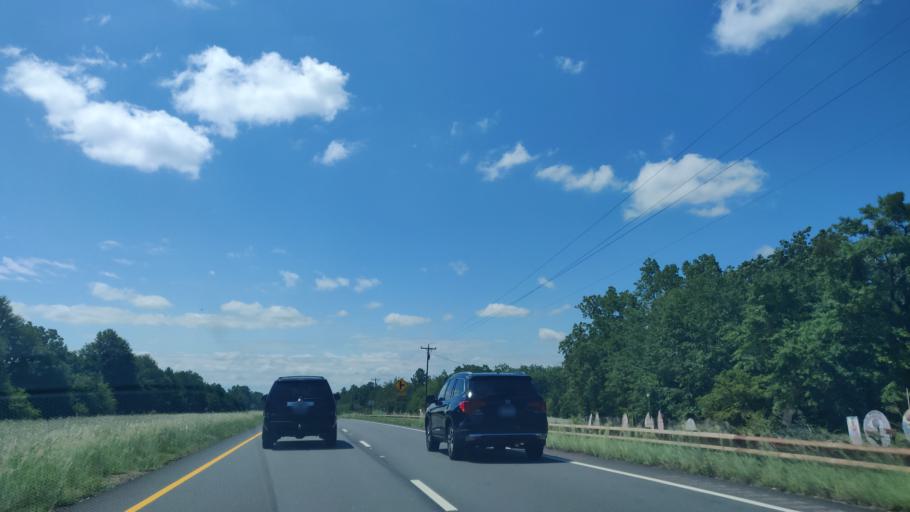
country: US
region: Georgia
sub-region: Stewart County
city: Richland
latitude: 32.1717
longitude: -84.7077
